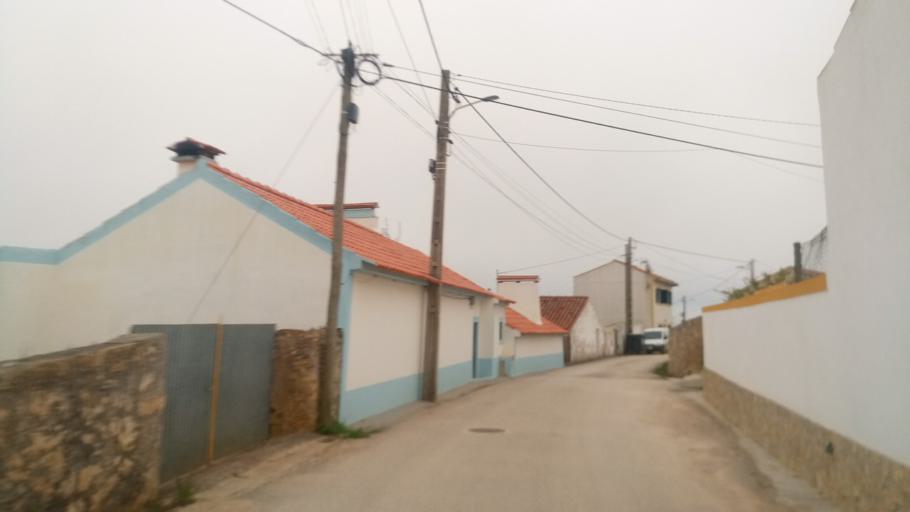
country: PT
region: Leiria
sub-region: Caldas da Rainha
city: Caldas da Rainha
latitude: 39.4620
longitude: -9.1932
